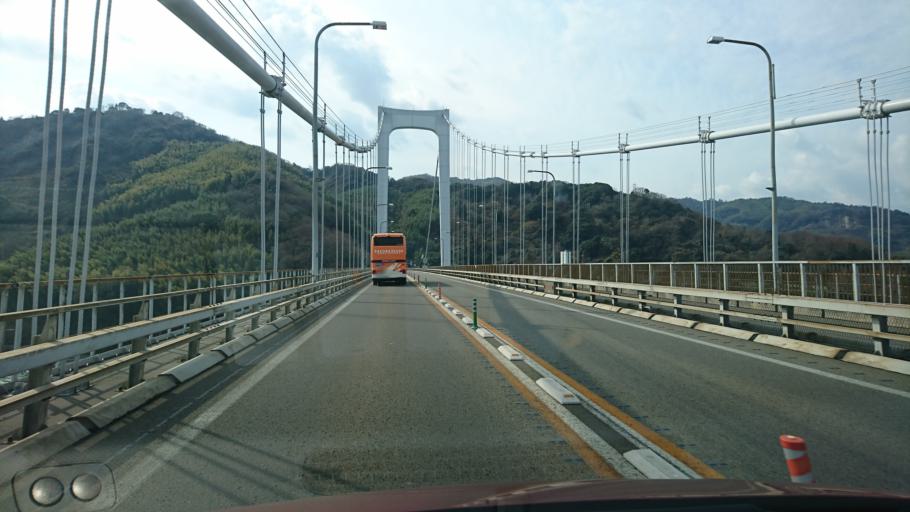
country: JP
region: Hiroshima
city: Innoshima
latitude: 34.1918
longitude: 133.0722
